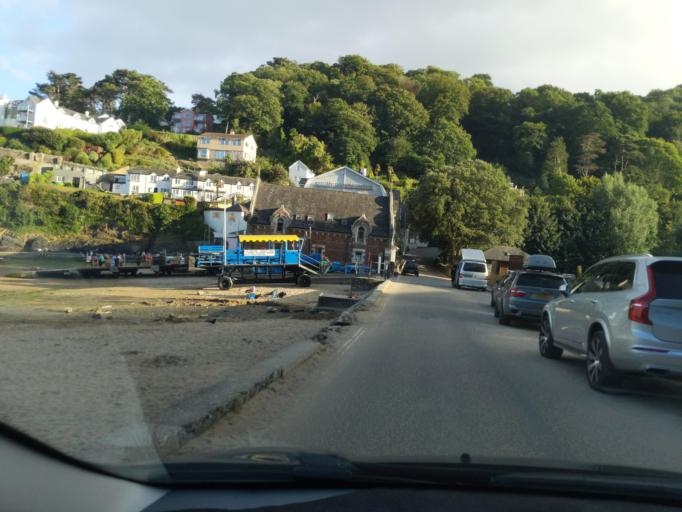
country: GB
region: England
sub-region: Devon
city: Salcombe
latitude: 50.2256
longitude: -3.7846
